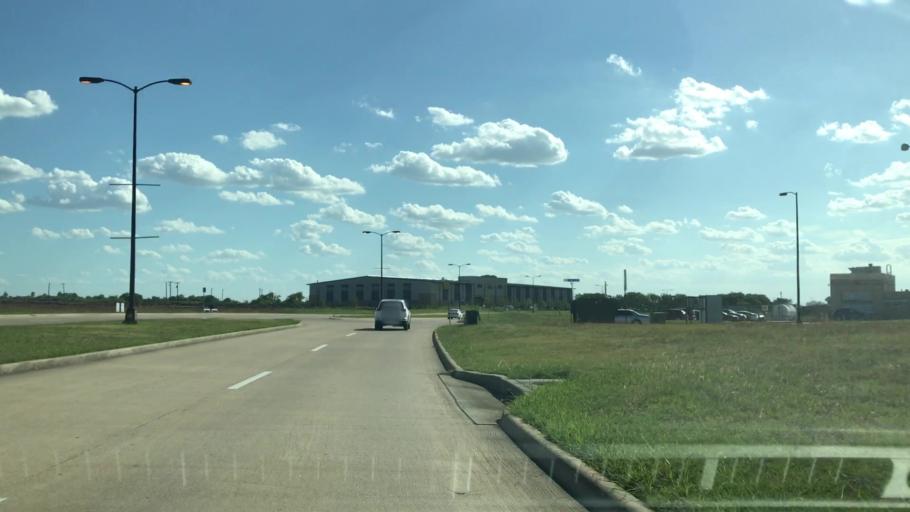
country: US
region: Texas
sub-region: Tarrant County
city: Euless
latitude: 32.8539
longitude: -97.0278
